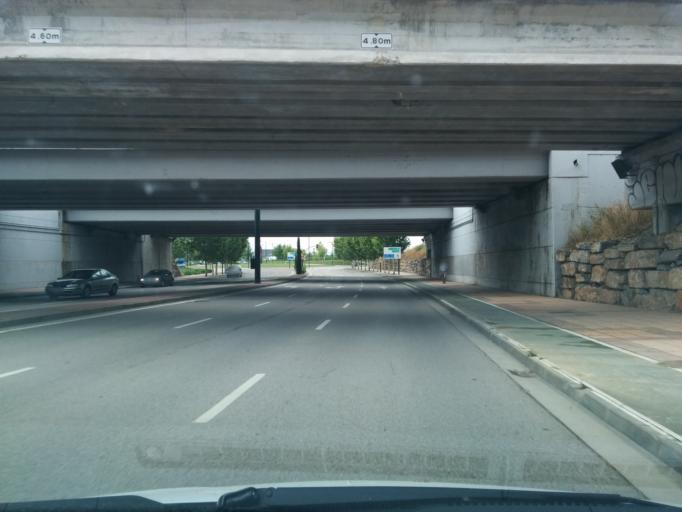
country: ES
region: Aragon
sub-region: Provincia de Zaragoza
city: Almozara
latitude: 41.6809
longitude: -0.8990
